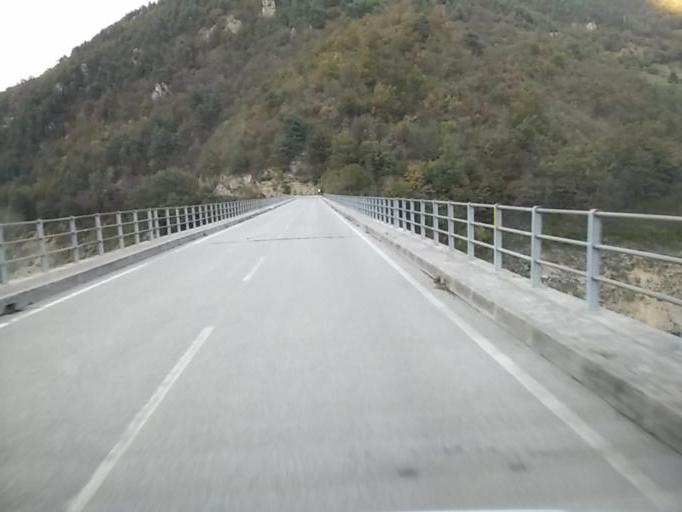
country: IT
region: Lombardy
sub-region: Provincia di Brescia
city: Valvestino
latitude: 45.7211
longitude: 10.6122
